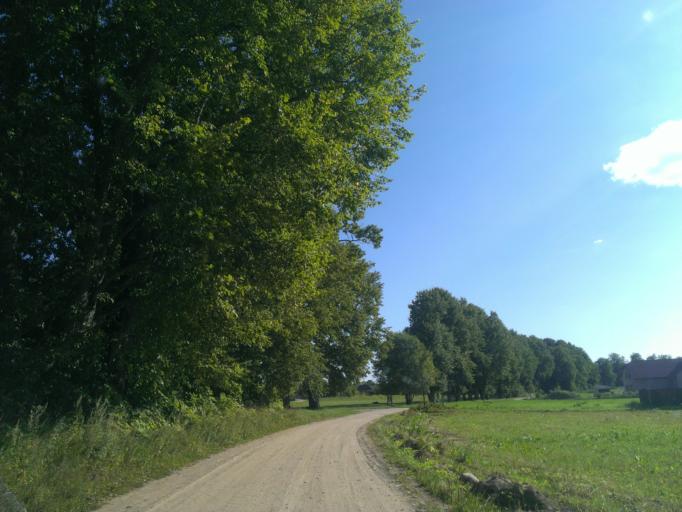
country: LV
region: Sigulda
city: Sigulda
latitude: 57.1682
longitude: 24.8884
